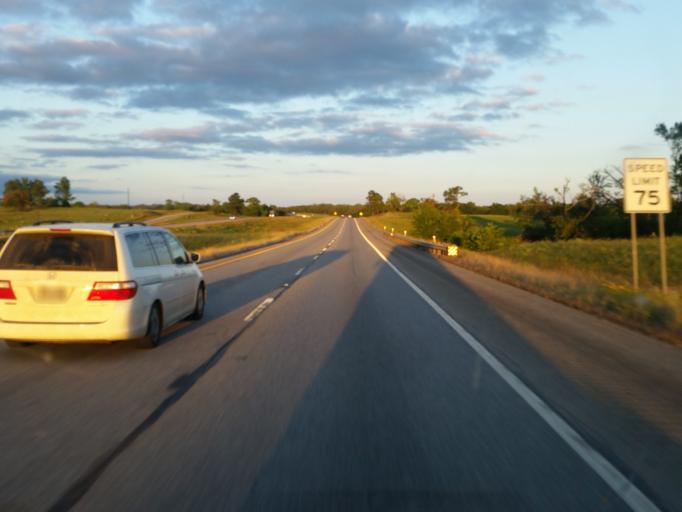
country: US
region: Texas
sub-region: Van Zandt County
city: Van
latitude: 32.5040
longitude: -95.6330
